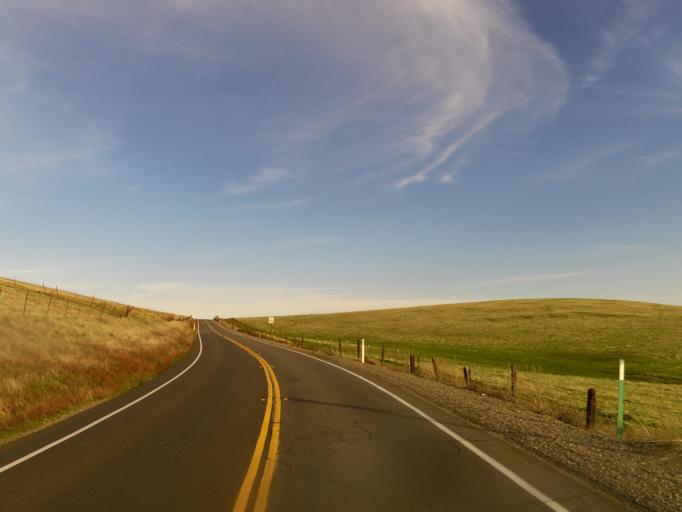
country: US
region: California
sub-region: El Dorado County
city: El Dorado Hills
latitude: 38.6278
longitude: -121.0870
